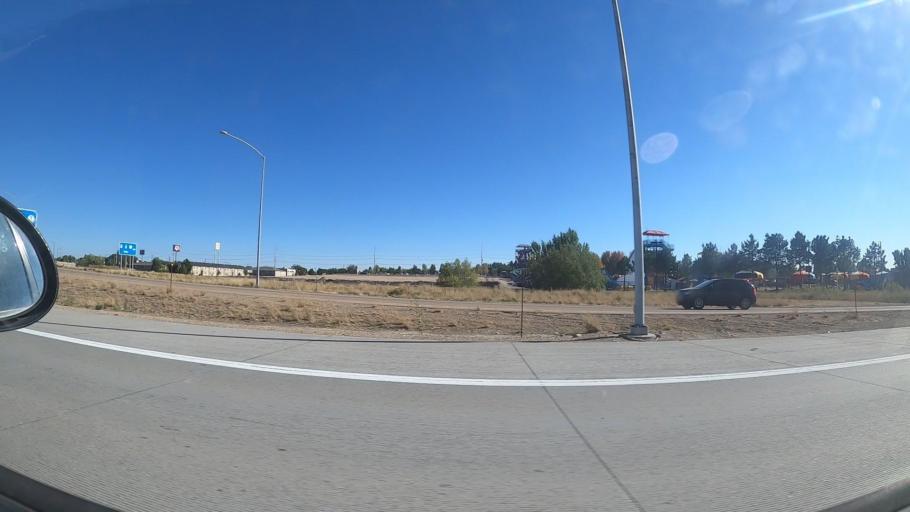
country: US
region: Idaho
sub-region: Ada County
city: Meridian
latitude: 43.5933
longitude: -116.4036
